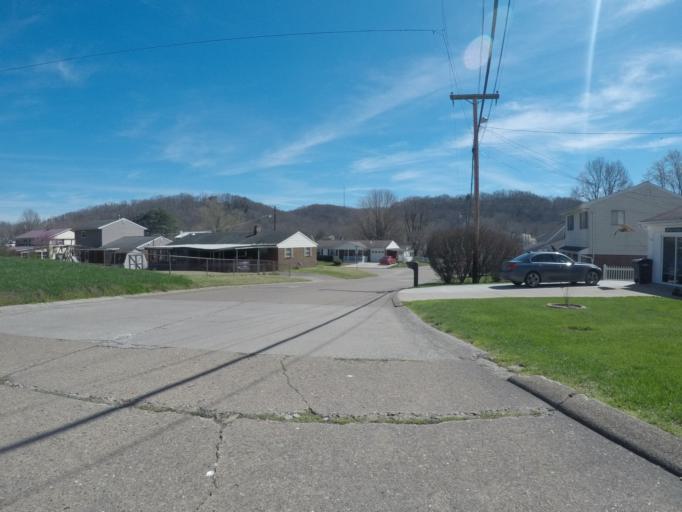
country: US
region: West Virginia
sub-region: Cabell County
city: Pea Ridge
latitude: 38.4002
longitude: -82.3196
